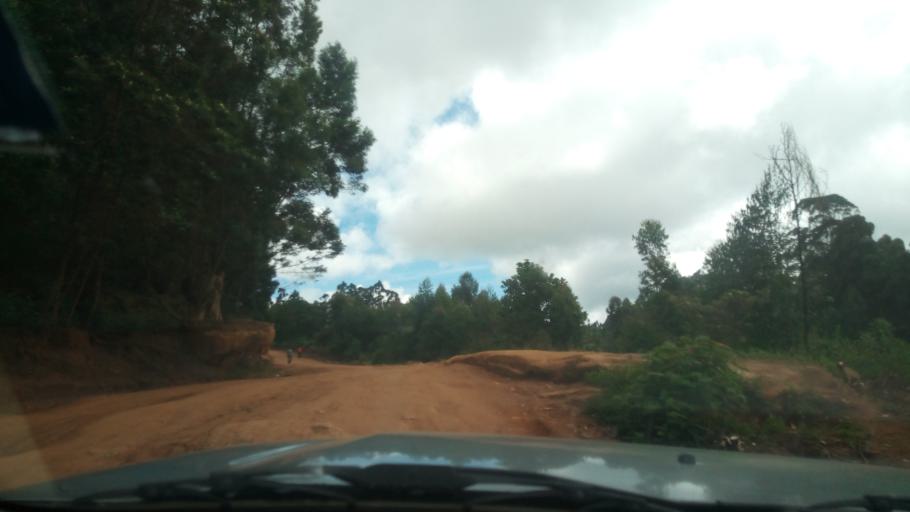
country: KE
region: Makueni
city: Wote
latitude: -1.6664
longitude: 37.4496
